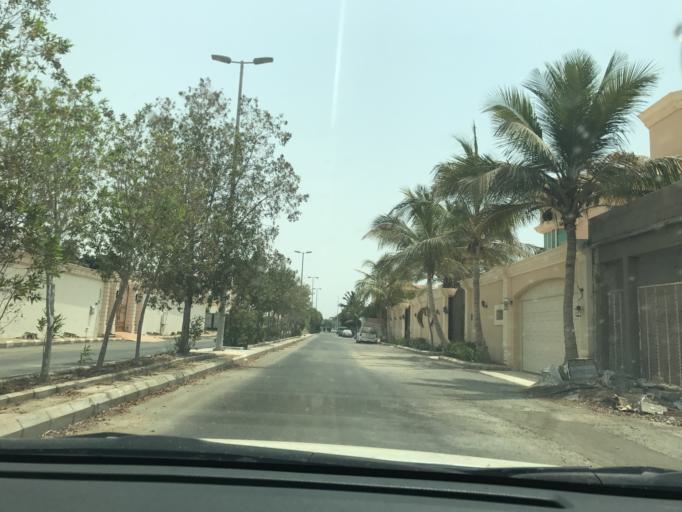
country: SA
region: Makkah
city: Jeddah
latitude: 21.6845
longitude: 39.1043
